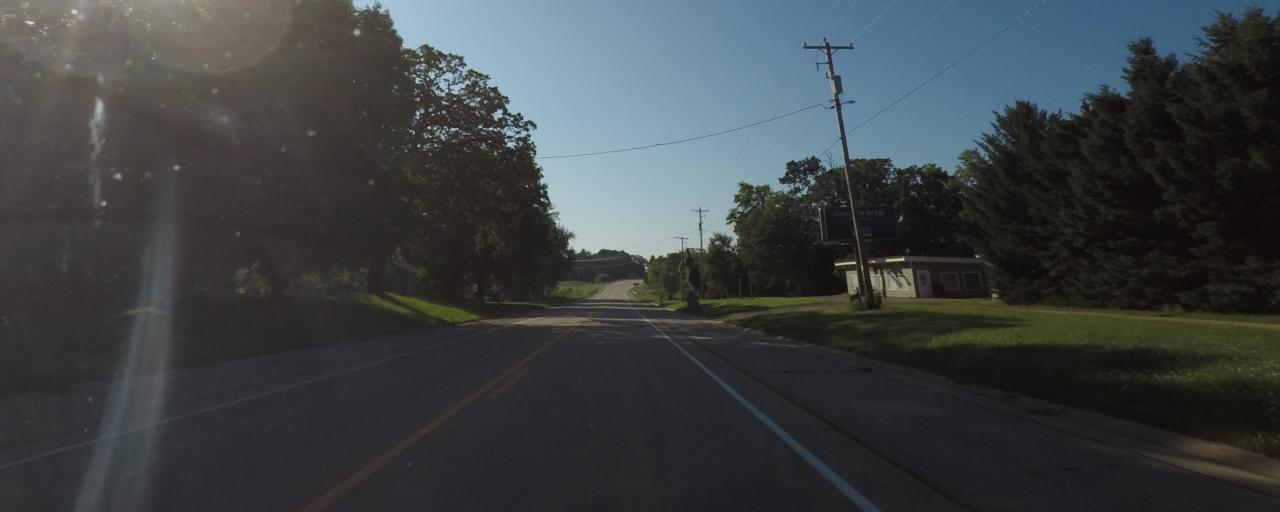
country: US
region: Wisconsin
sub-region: Jefferson County
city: Lake Koshkonong
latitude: 42.9575
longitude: -88.8884
